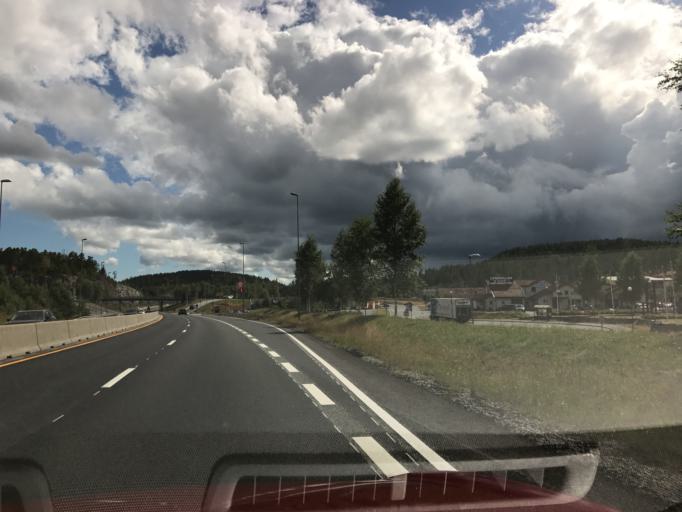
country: NO
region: Aust-Agder
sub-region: Gjerstad
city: Gjerstad
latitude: 58.8239
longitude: 9.0757
